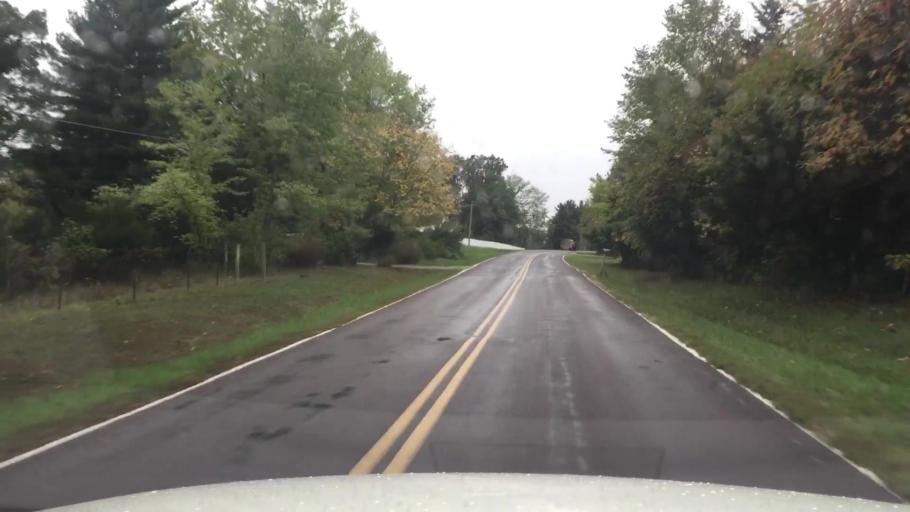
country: US
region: Missouri
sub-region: Boone County
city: Ashland
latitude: 38.7106
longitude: -92.2856
